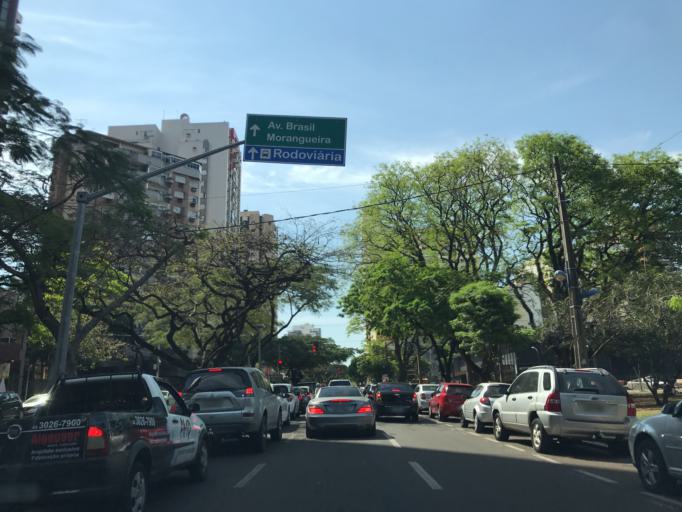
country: BR
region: Parana
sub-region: Maringa
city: Maringa
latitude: -23.4245
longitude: -51.9331
